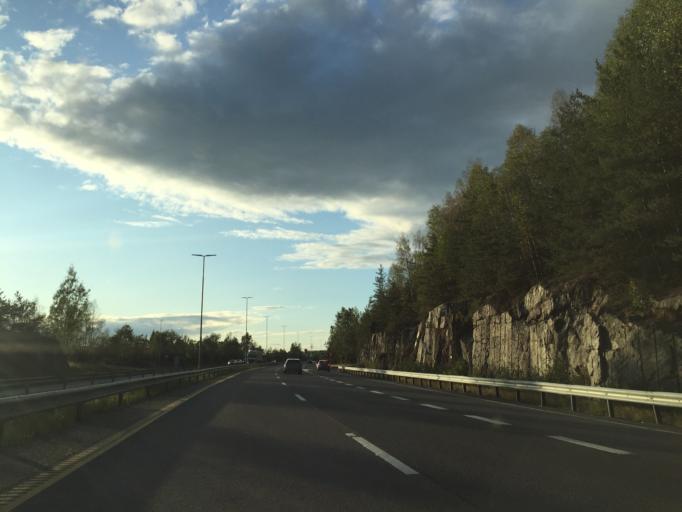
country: NO
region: Akershus
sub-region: Lorenskog
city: Kjenn
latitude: 59.9307
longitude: 10.9467
